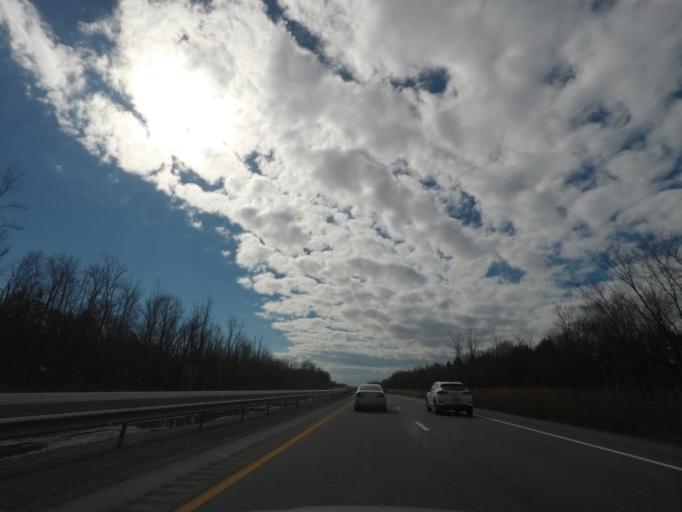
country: US
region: New York
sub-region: Madison County
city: Oneida
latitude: 43.1253
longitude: -75.6137
